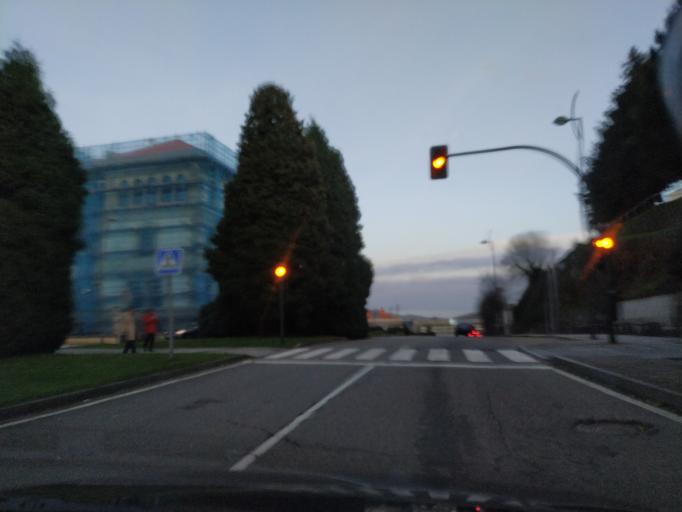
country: ES
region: Galicia
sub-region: Provincia da Coruna
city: Santiago de Compostela
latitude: 42.8884
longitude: -8.5360
